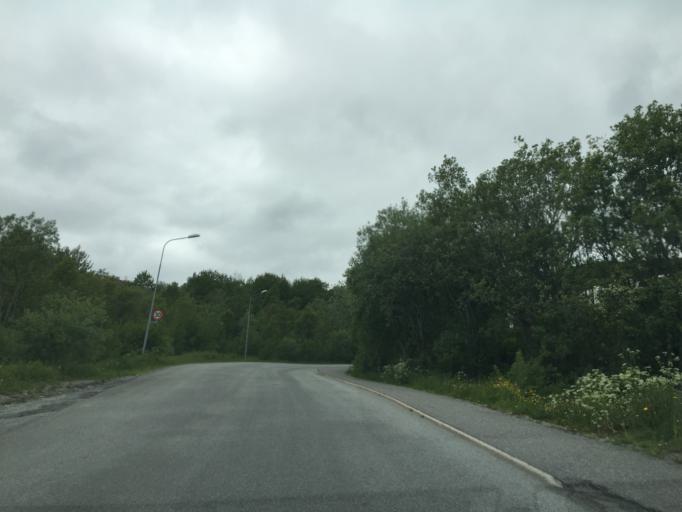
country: NO
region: Nordland
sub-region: Bodo
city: Lopsmarka
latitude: 67.2819
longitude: 14.5293
